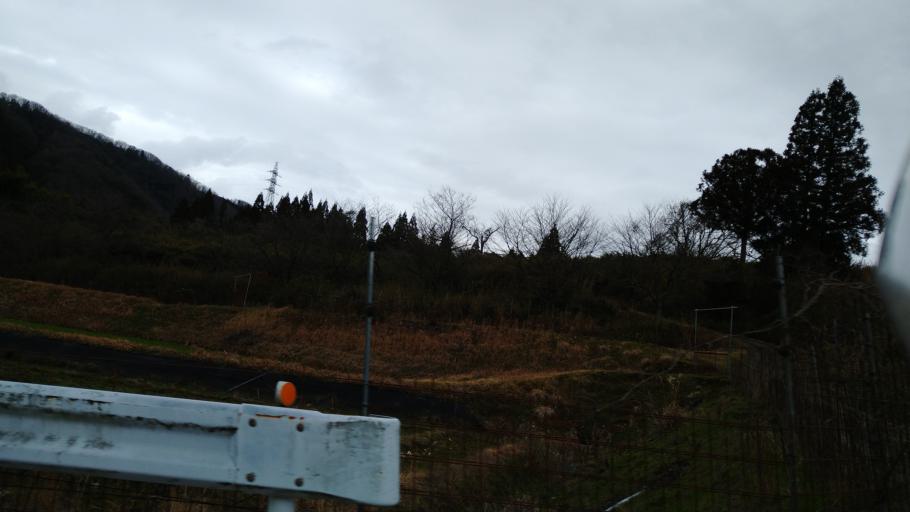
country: JP
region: Kyoto
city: Ayabe
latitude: 35.3240
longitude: 135.3580
